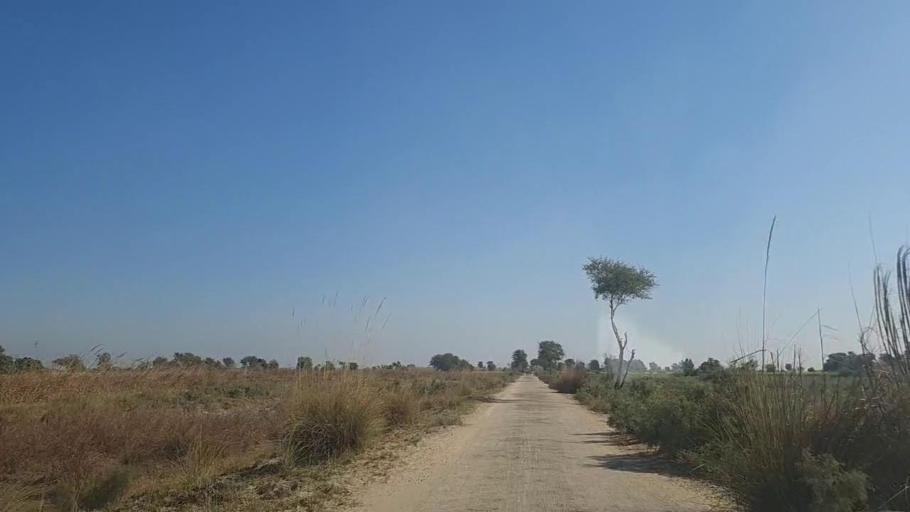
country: PK
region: Sindh
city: Sinjhoro
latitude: 26.1589
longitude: 68.8556
